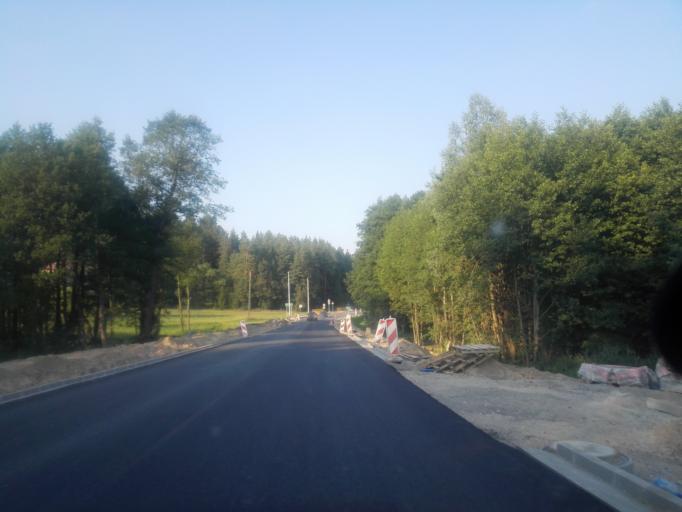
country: PL
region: Podlasie
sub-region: Powiat sejnenski
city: Krasnopol
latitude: 54.0819
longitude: 23.0775
